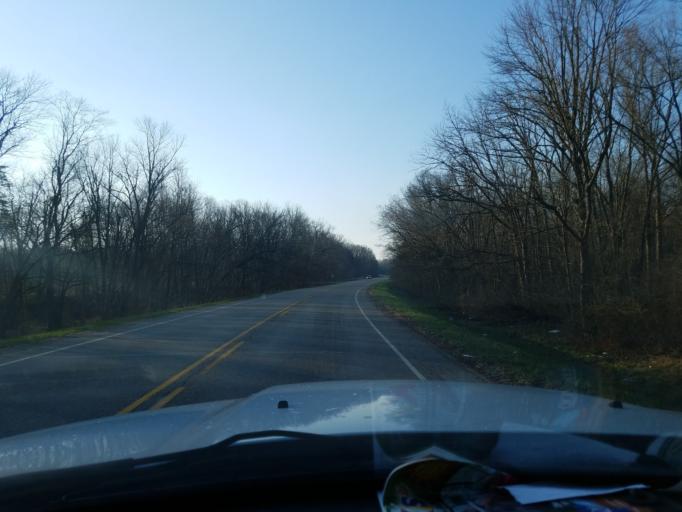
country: US
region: Indiana
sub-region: Vigo County
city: Seelyville
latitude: 39.4056
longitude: -87.3222
